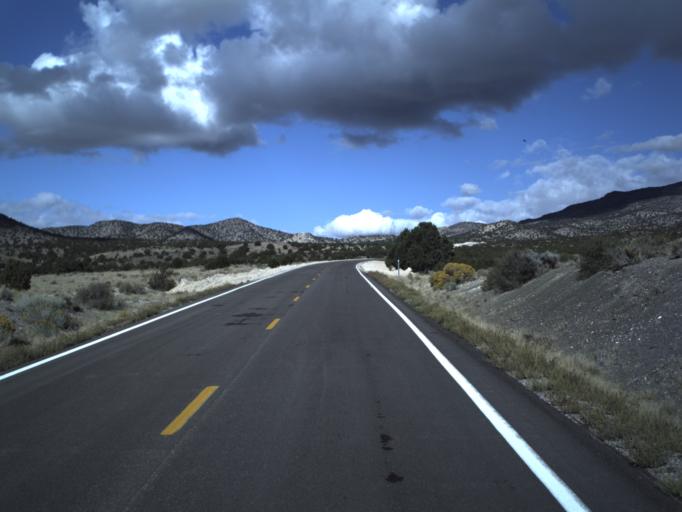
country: US
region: Utah
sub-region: Beaver County
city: Milford
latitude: 38.5026
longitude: -113.5058
